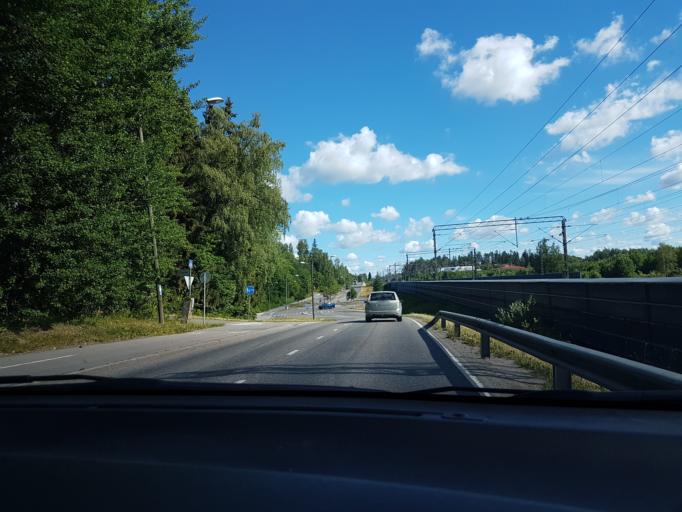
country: FI
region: Uusimaa
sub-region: Helsinki
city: Kerava
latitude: 60.3736
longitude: 25.0948
